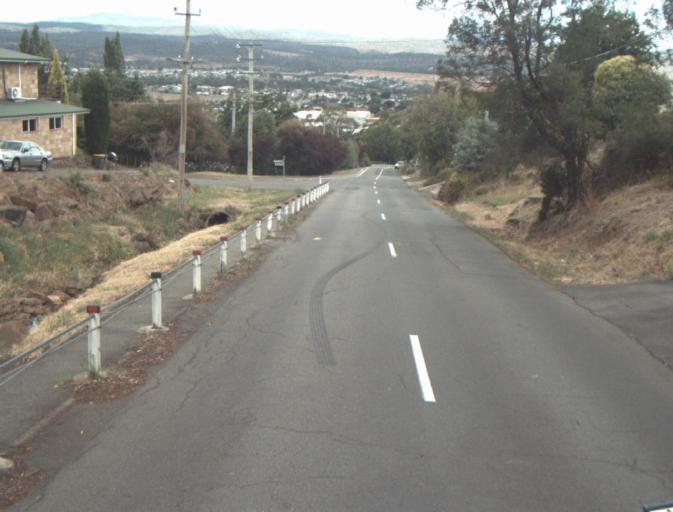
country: AU
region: Tasmania
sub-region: Launceston
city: Launceston
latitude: -41.4296
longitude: 147.1140
